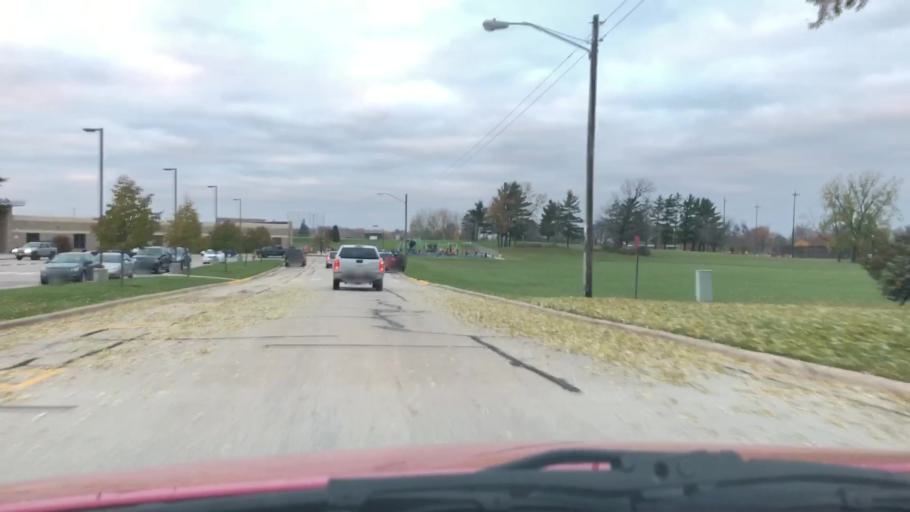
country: US
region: Wisconsin
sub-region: Outagamie County
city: Seymour
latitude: 44.5056
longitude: -88.3334
